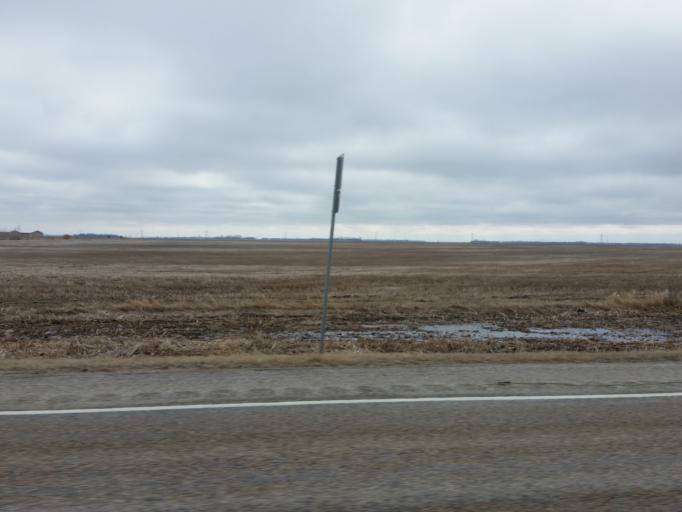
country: US
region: North Dakota
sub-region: Cass County
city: Casselton
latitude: 46.8573
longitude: -97.2181
